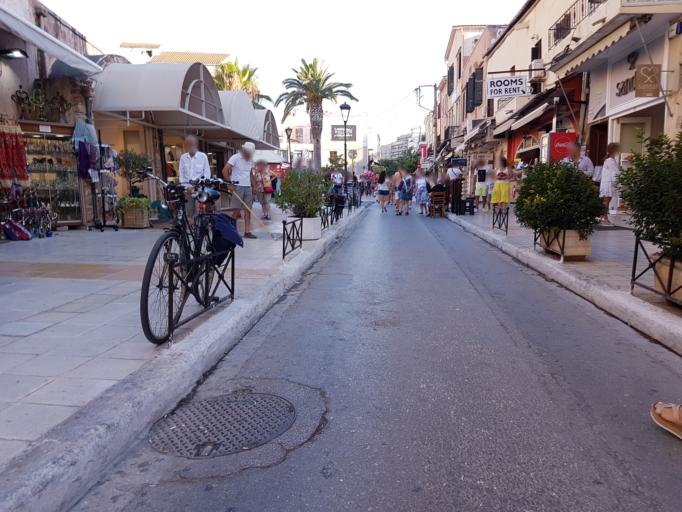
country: GR
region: Crete
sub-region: Nomos Chanias
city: Chania
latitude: 35.5158
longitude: 24.0176
